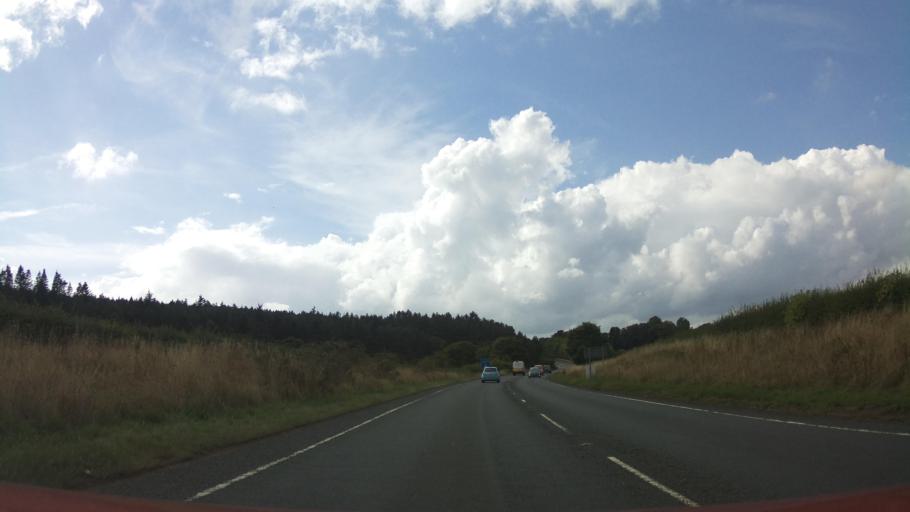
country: GB
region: England
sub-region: Northumberland
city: Healey
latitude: 54.9473
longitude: -1.9572
